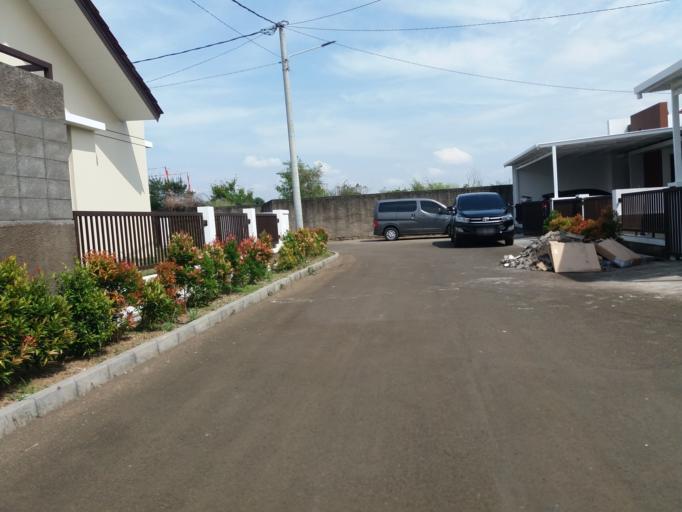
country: ID
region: West Java
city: Bandung
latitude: -6.9216
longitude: 107.6656
